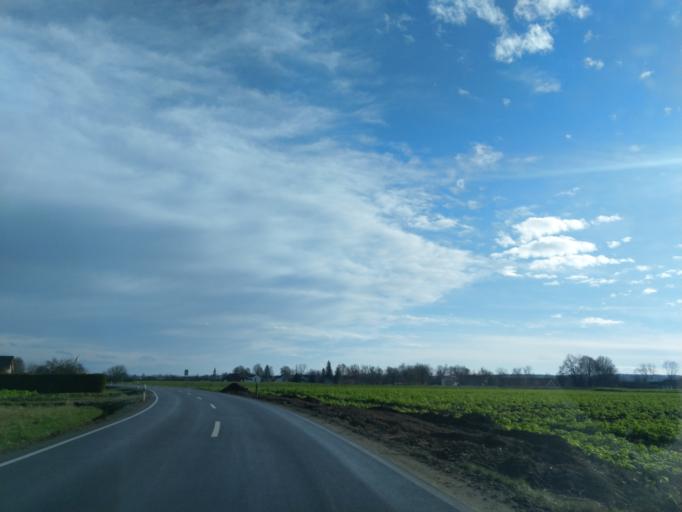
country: DE
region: Bavaria
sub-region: Lower Bavaria
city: Rossbach
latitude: 48.6247
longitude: 12.9647
